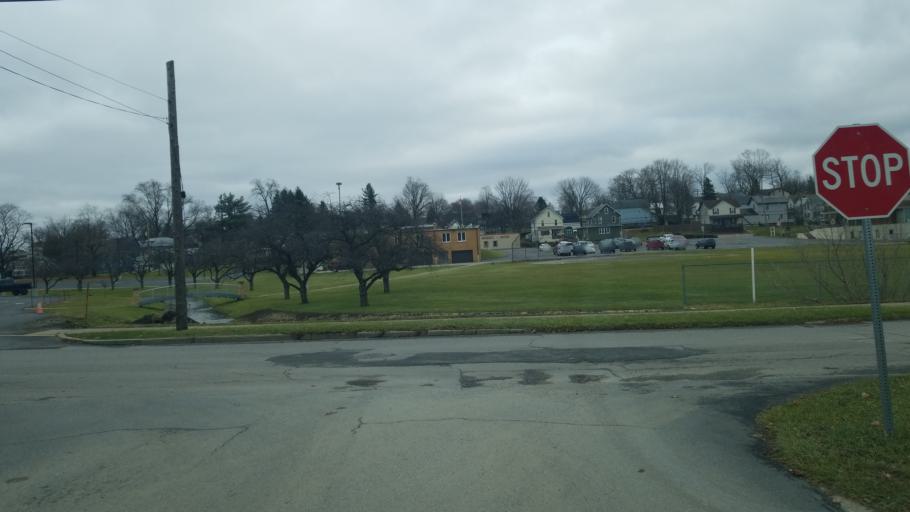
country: US
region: Pennsylvania
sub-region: Clearfield County
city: DuBois
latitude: 41.1305
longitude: -78.7597
